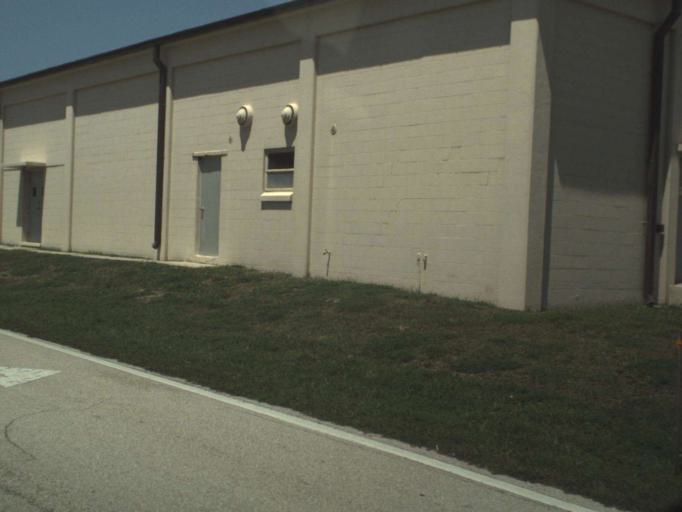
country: US
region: Florida
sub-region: Brevard County
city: South Patrick Shores
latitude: 28.2274
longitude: -80.6001
